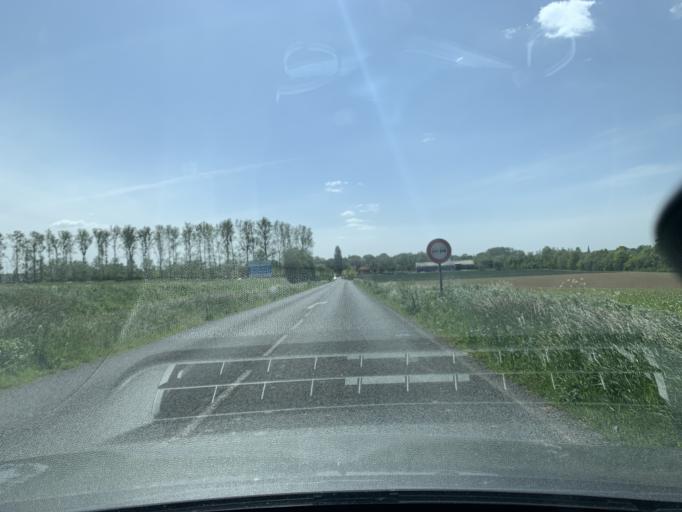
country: FR
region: Nord-Pas-de-Calais
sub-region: Departement du Nord
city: Masnieres
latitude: 50.1319
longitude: 3.1950
